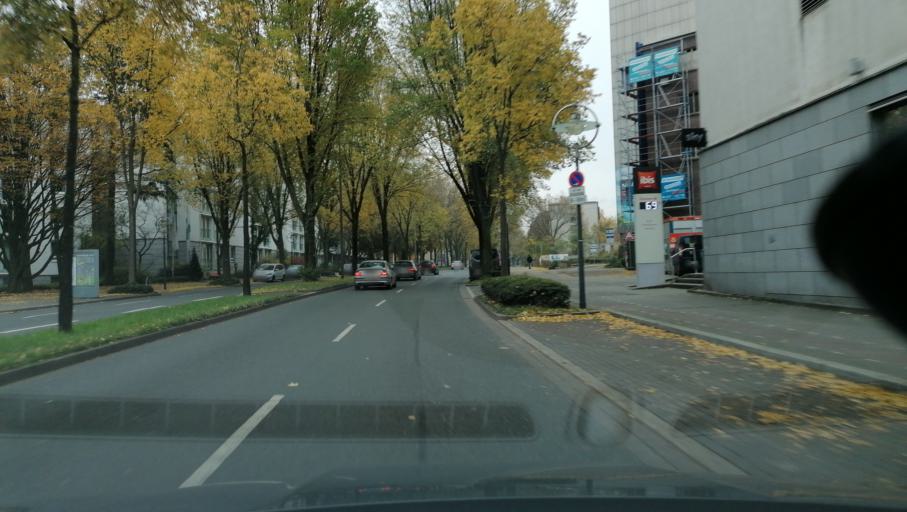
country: DE
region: North Rhine-Westphalia
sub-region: Regierungsbezirk Arnsberg
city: Dortmund
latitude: 51.5042
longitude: 7.4767
